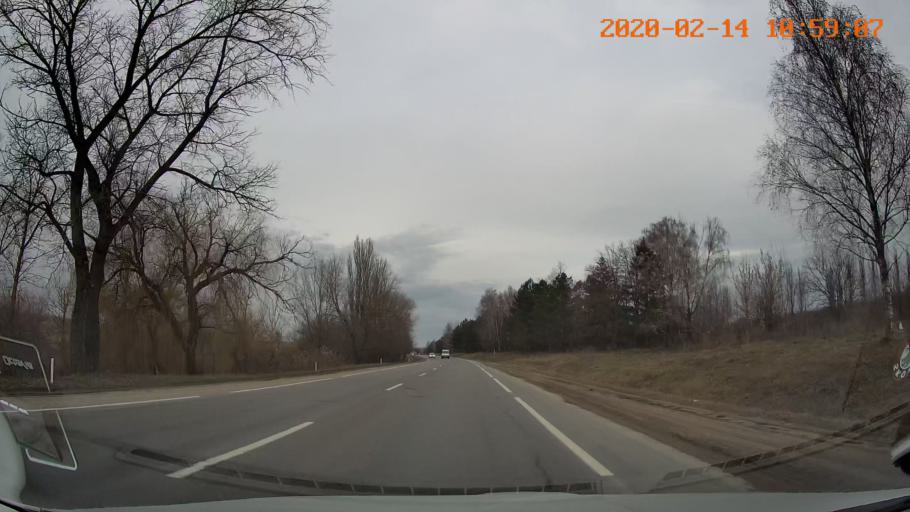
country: MD
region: Raionul Edinet
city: Edinet
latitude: 48.1392
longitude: 27.3558
